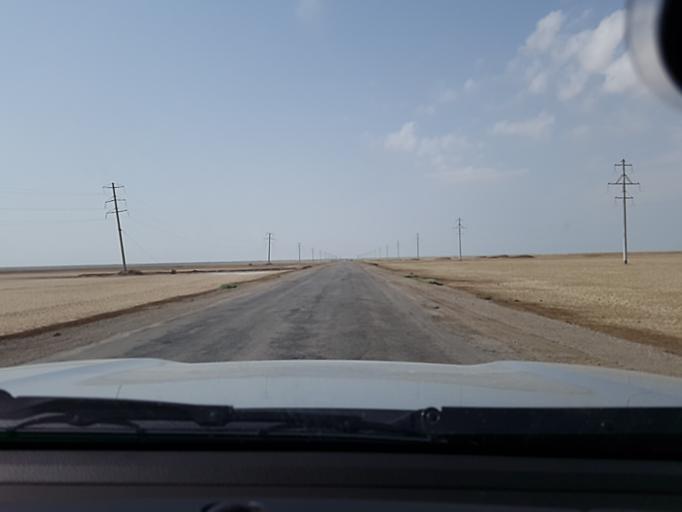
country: TM
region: Balkan
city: Gumdag
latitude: 39.0781
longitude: 54.5843
